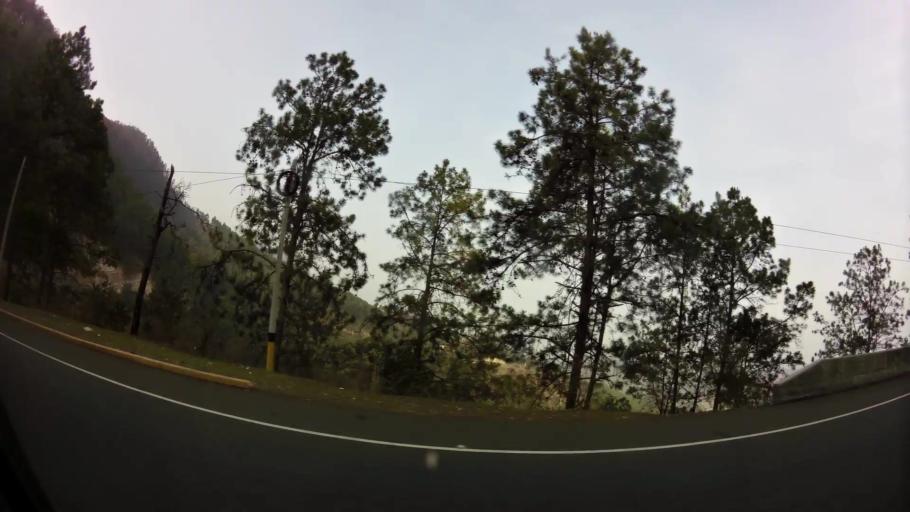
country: HN
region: Comayagua
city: Flores
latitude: 14.2882
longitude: -87.4908
